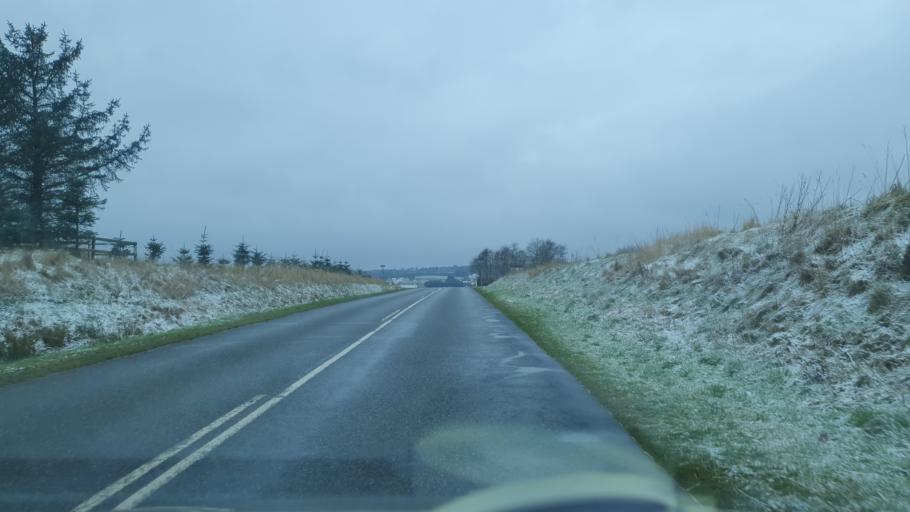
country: DK
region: North Denmark
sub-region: Jammerbugt Kommune
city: Brovst
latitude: 57.1261
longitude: 9.4825
